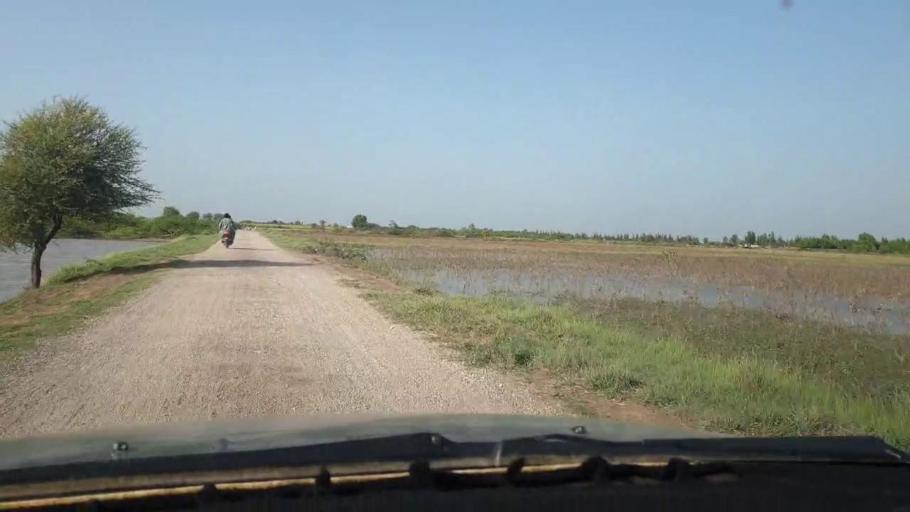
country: PK
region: Sindh
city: Chambar
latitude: 25.2757
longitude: 68.9234
